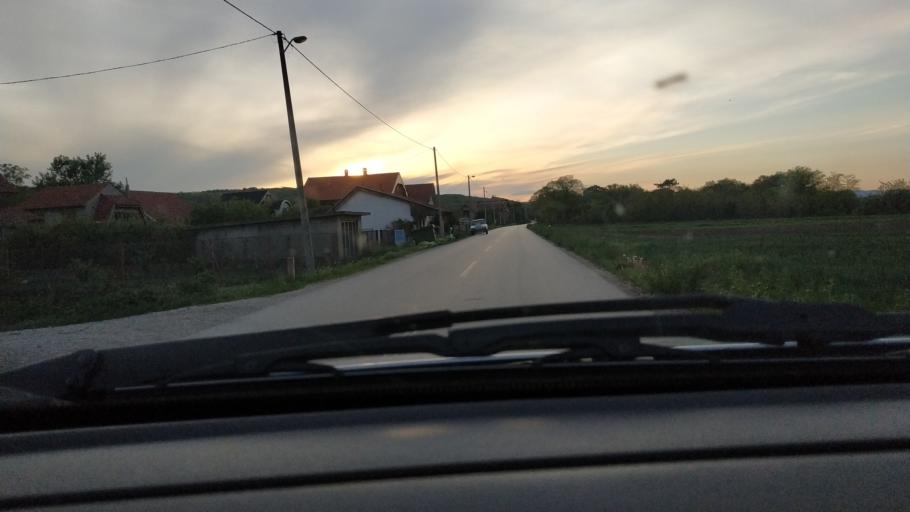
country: RS
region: Central Serbia
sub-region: Nisavski Okrug
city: Aleksinac
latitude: 43.5514
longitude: 21.6171
